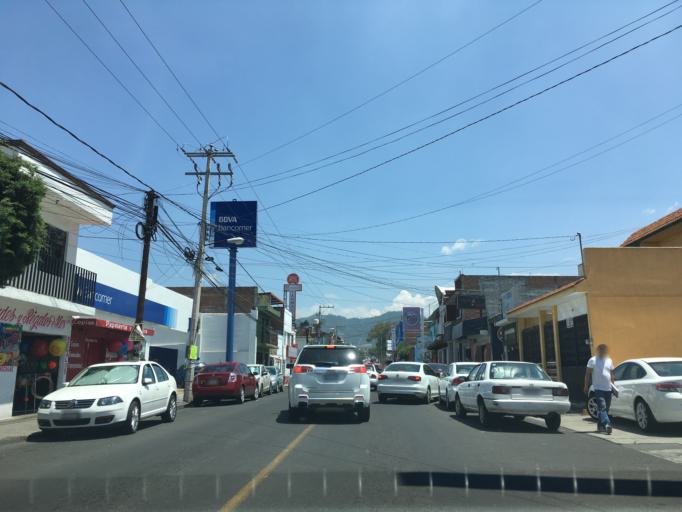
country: MX
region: Michoacan
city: Morelia
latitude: 19.7026
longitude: -101.1716
